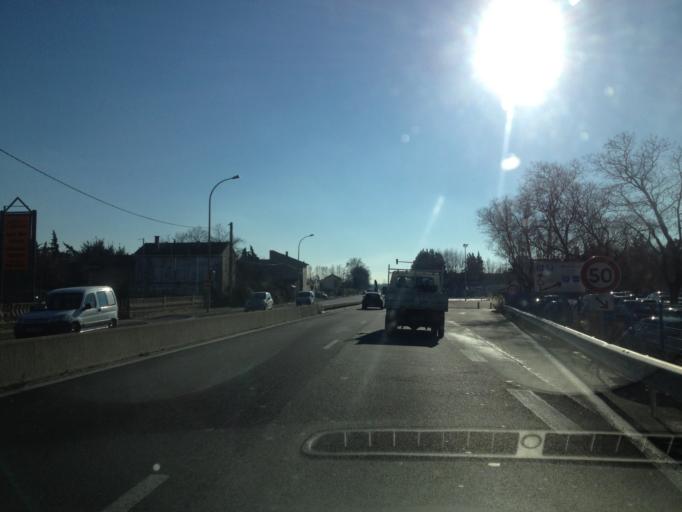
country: FR
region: Provence-Alpes-Cote d'Azur
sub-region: Departement du Vaucluse
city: Sorgues
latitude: 43.9937
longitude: 4.8649
